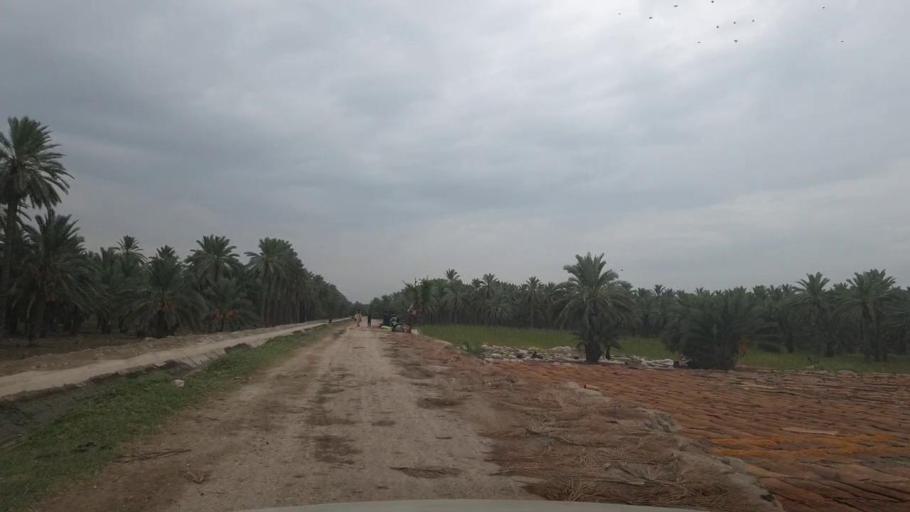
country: PK
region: Sindh
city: Khairpur
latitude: 27.6038
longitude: 68.8159
